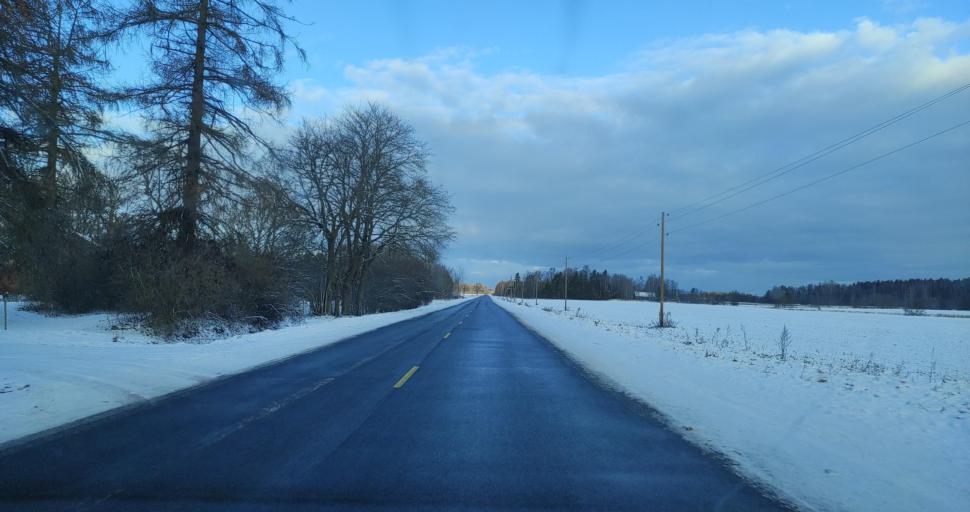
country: LV
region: Skrunda
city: Skrunda
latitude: 56.7348
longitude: 22.0001
